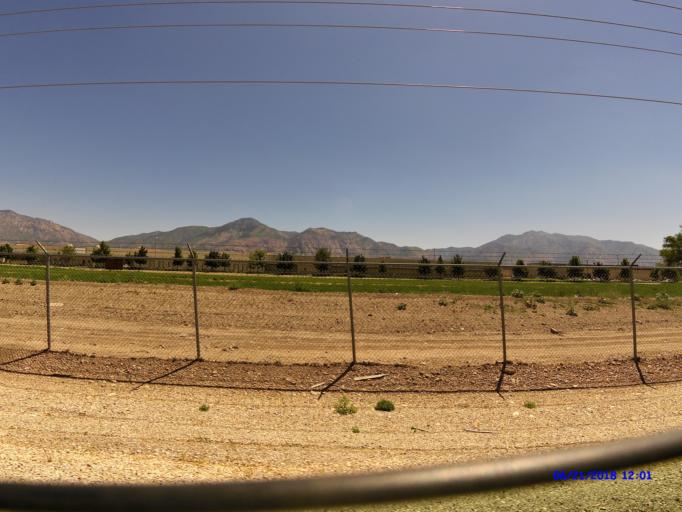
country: US
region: Utah
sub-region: Weber County
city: Marriott-Slaterville
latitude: 41.2638
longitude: -112.0089
